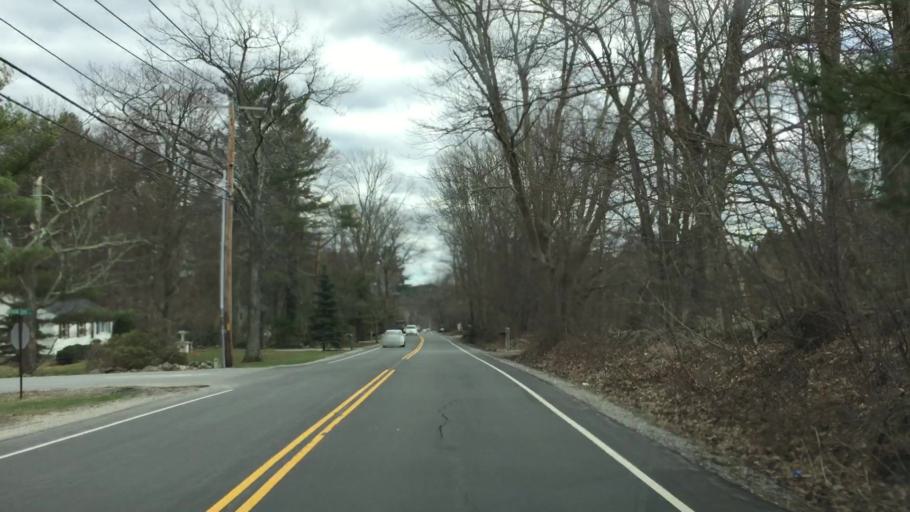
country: US
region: New Hampshire
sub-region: Rockingham County
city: Windham
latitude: 42.8114
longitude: -71.3569
